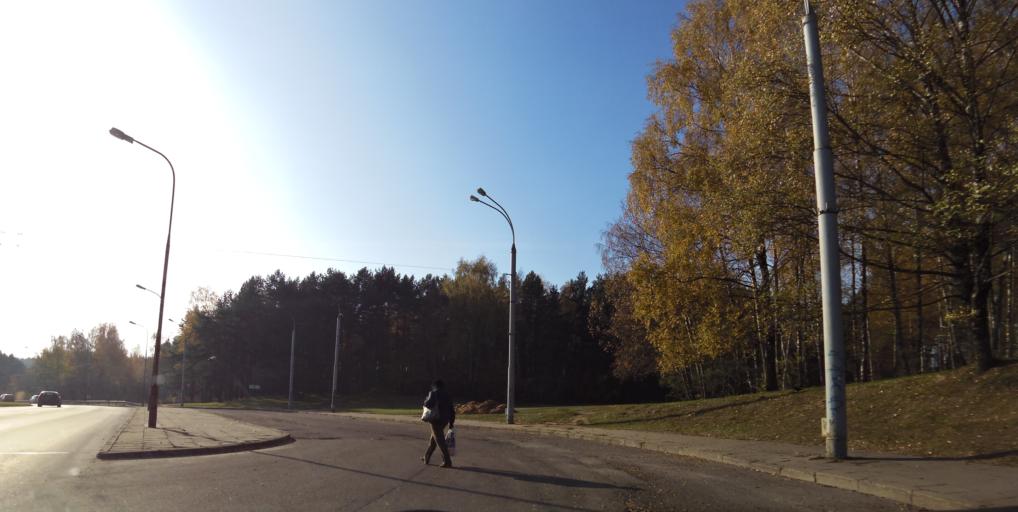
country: LT
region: Vilnius County
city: Lazdynai
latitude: 54.6833
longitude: 25.2068
